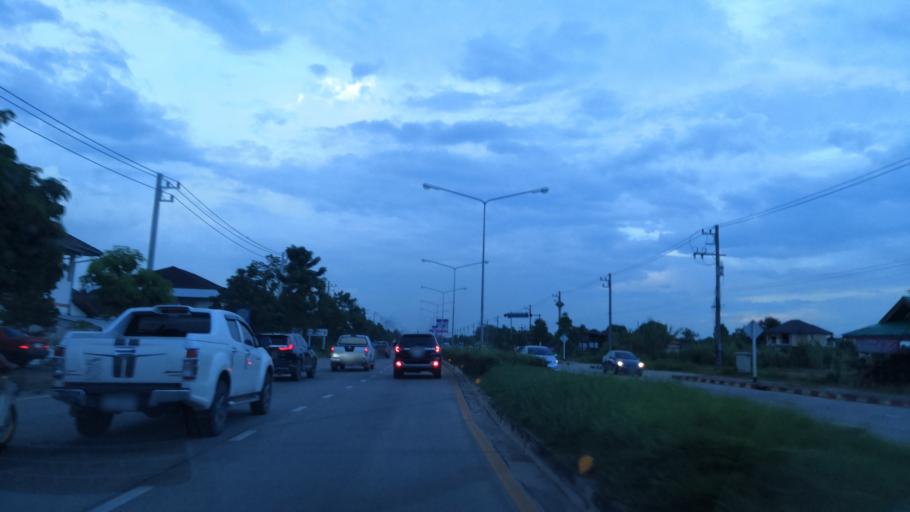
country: TH
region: Chiang Rai
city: Chiang Rai
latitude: 19.8956
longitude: 99.8564
